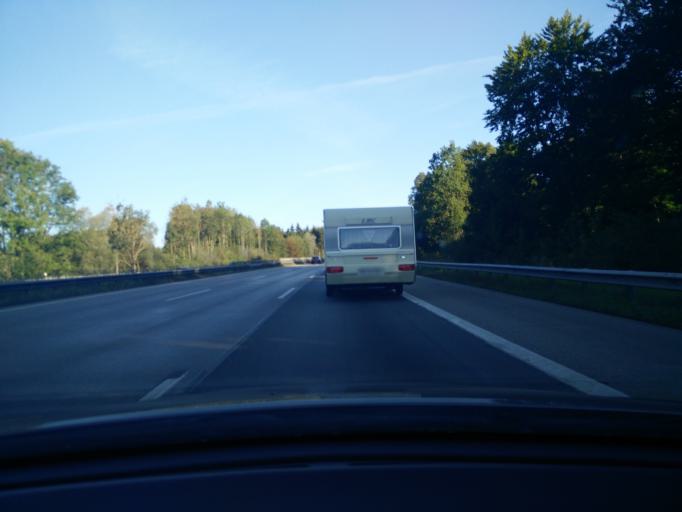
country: DE
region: Bavaria
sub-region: Upper Bavaria
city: Vagen
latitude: 47.8423
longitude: 11.8694
